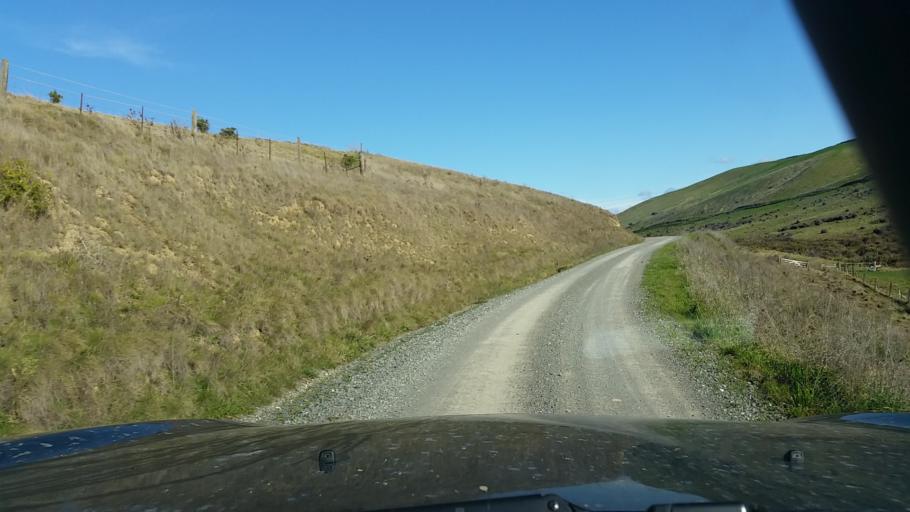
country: NZ
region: Marlborough
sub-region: Marlborough District
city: Blenheim
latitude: -41.6676
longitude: 174.1399
